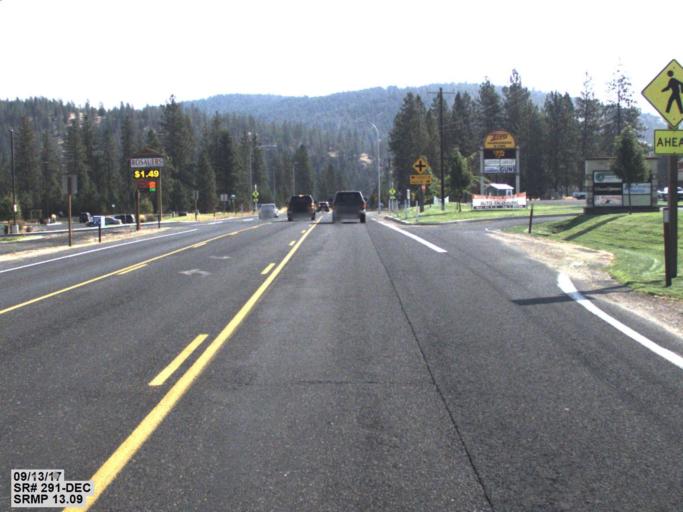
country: US
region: Washington
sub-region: Spokane County
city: Fairwood
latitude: 47.8115
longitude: -117.5637
